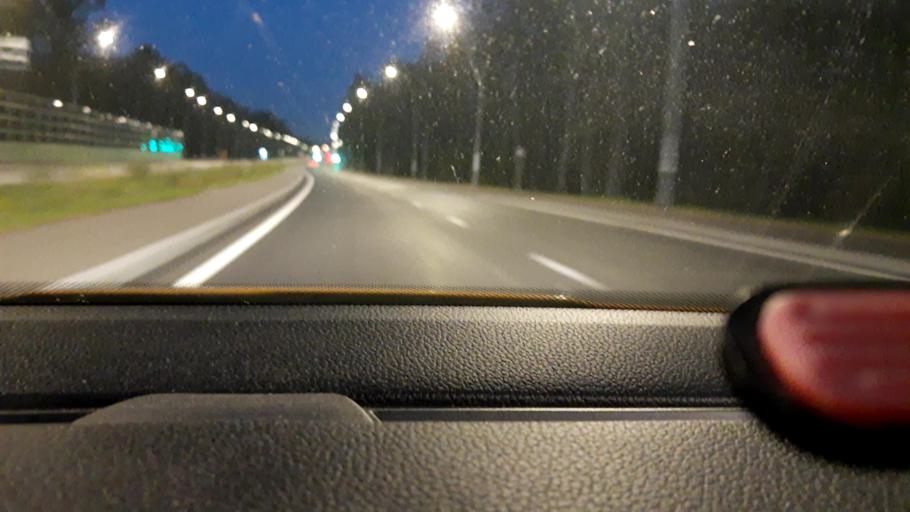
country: RU
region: Moskovskaya
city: Moskovskiy
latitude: 55.5879
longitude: 37.4026
